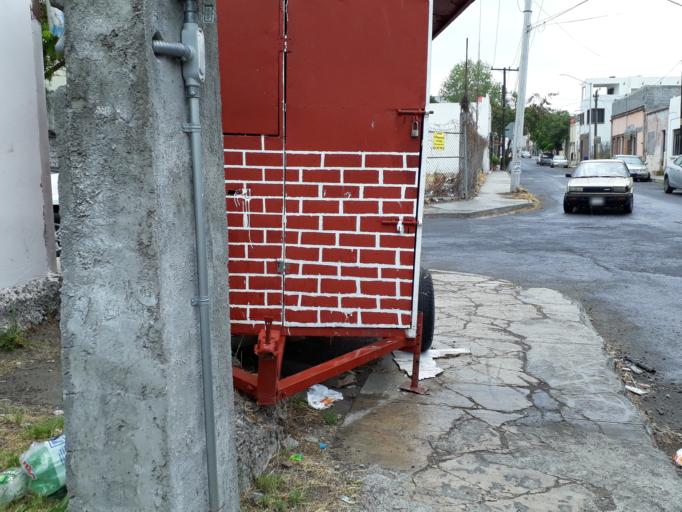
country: MX
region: Nuevo Leon
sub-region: Monterrey
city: Monterrey
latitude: 25.6698
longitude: -100.3025
